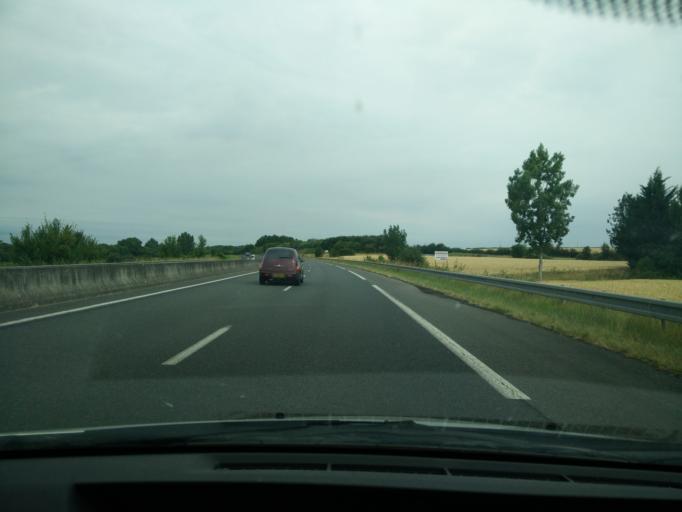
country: FR
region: Pays de la Loire
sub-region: Departement de Maine-et-Loire
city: Saint-Jean
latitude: 47.2436
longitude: -0.3214
